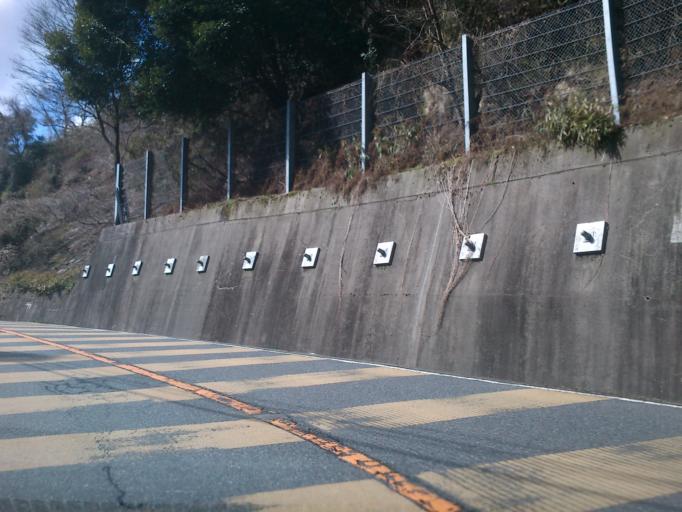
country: JP
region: Shiga Prefecture
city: Otsu-shi
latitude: 35.0354
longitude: 135.8380
